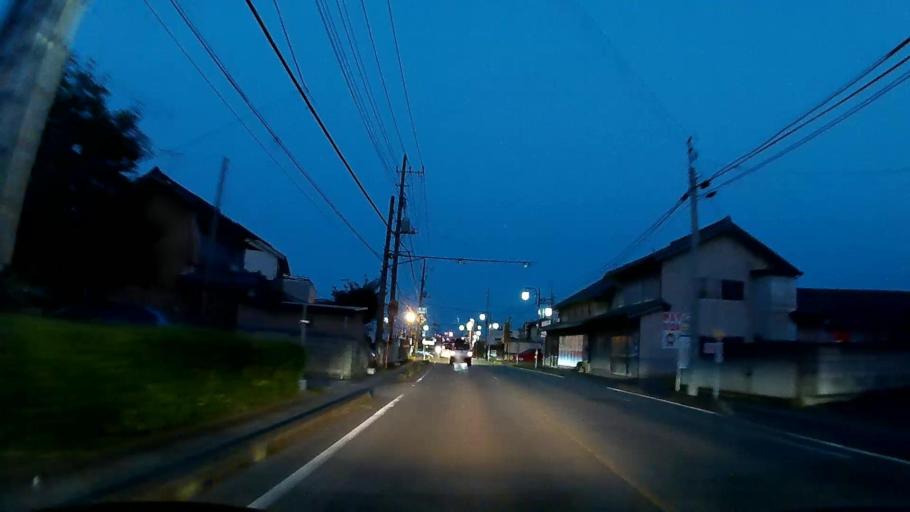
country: JP
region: Gunma
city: Takasaki
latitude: 36.3330
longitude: 138.9858
